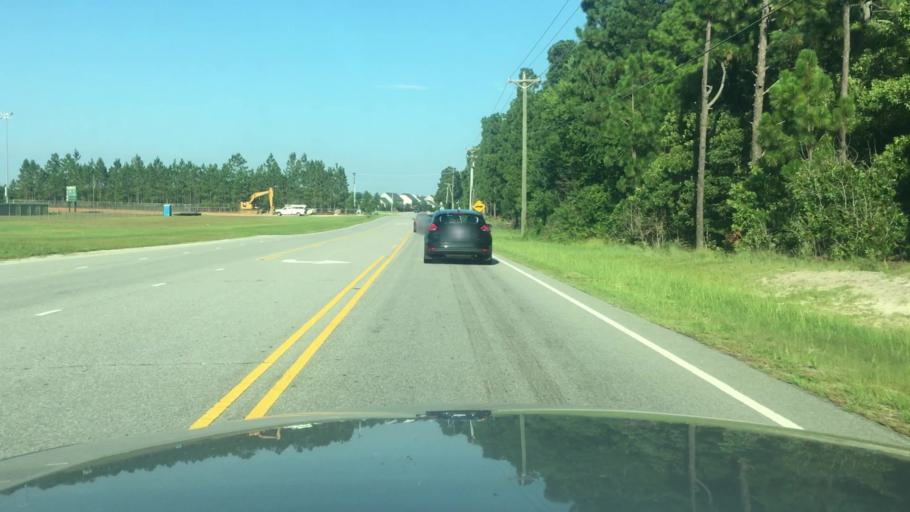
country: US
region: North Carolina
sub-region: Cumberland County
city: Spring Lake
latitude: 35.1558
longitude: -78.8885
